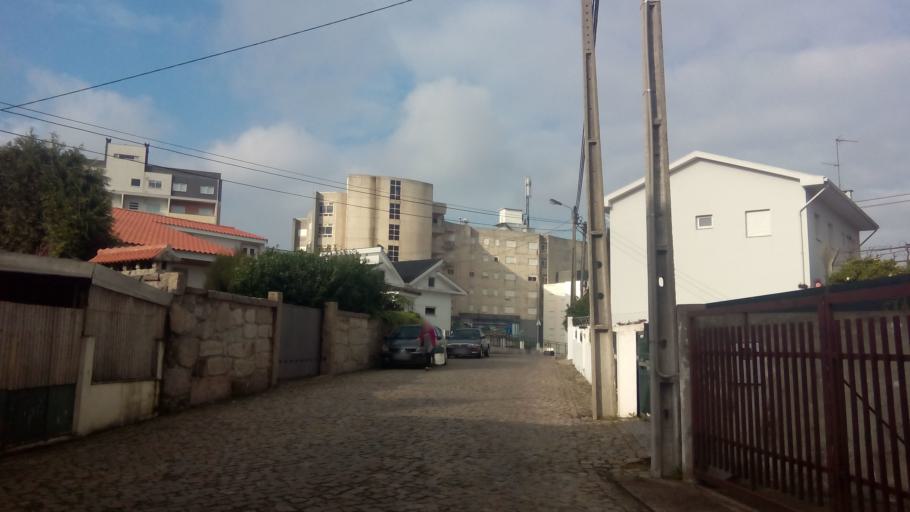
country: PT
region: Porto
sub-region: Paredes
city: Paredes
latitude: 41.2022
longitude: -8.3252
